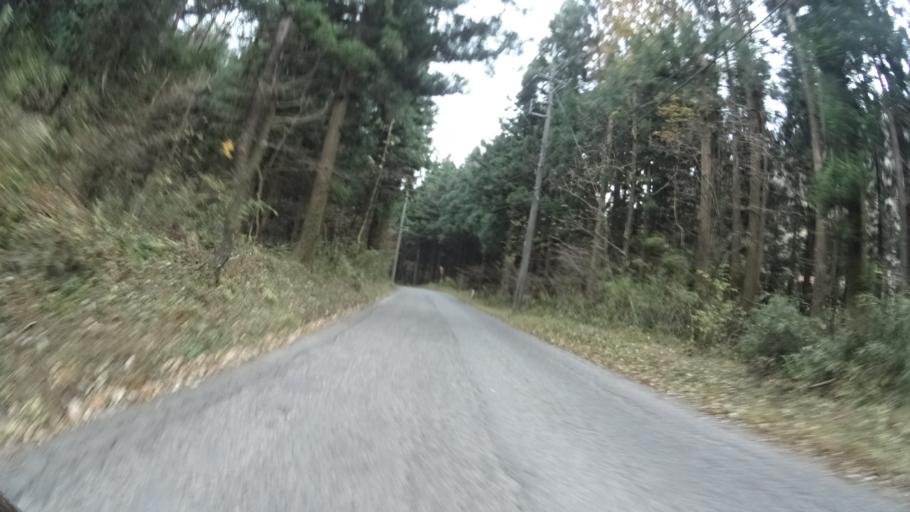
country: JP
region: Gunma
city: Omamacho-omama
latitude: 36.4895
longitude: 139.1854
